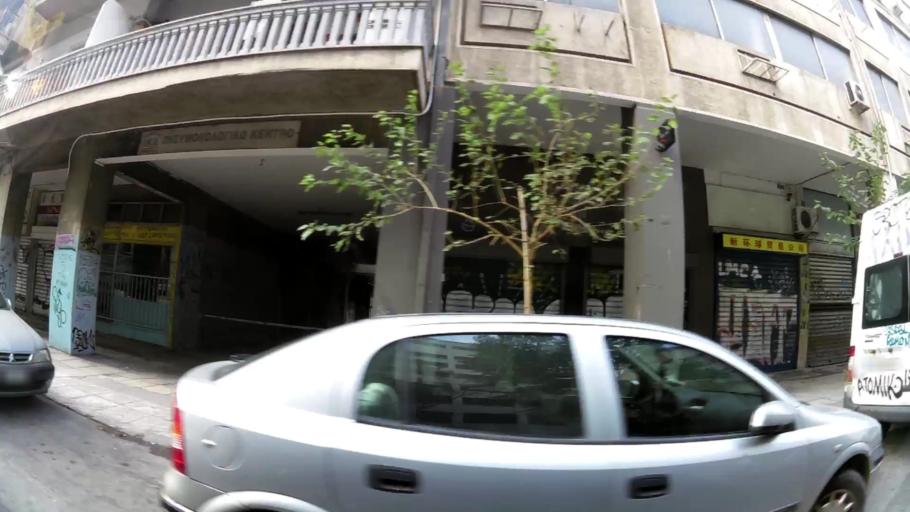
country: GR
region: Attica
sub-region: Nomarchia Athinas
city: Athens
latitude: 37.9811
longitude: 23.7204
